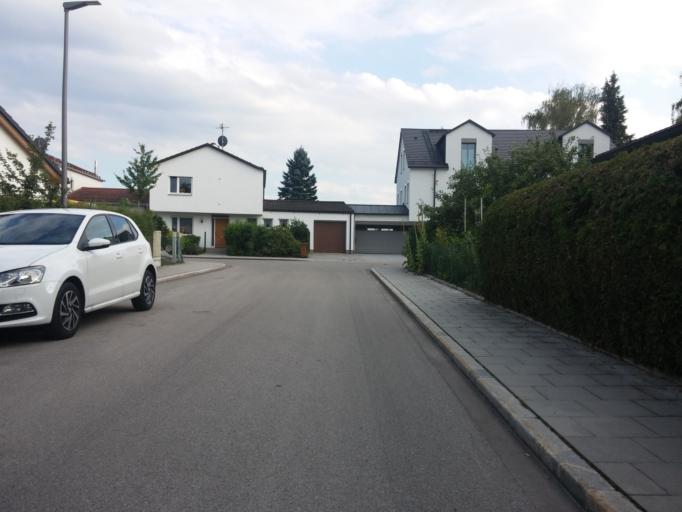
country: DE
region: Bavaria
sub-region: Upper Bavaria
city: Haar
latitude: 48.1023
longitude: 11.7339
